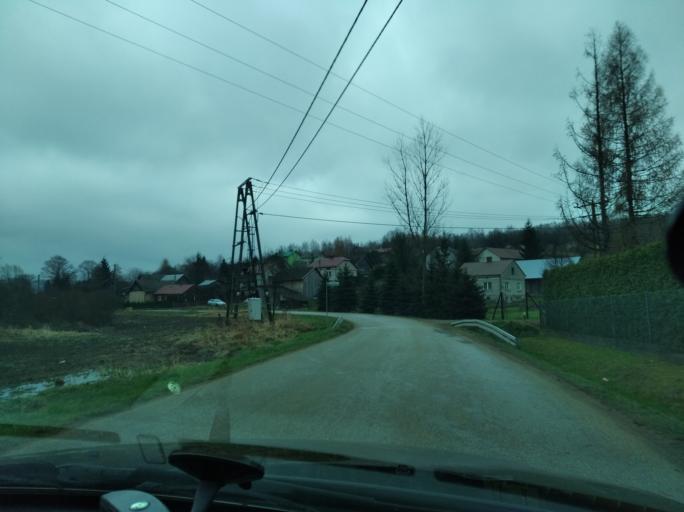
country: PL
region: Subcarpathian Voivodeship
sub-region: Powiat przeworski
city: Jawornik Polski
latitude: 49.9097
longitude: 22.2827
